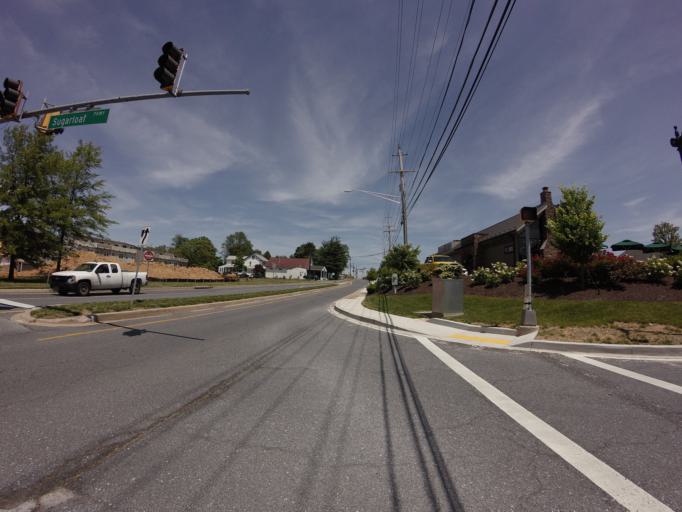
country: US
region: Maryland
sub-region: Frederick County
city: Urbana
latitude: 39.3260
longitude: -77.3501
